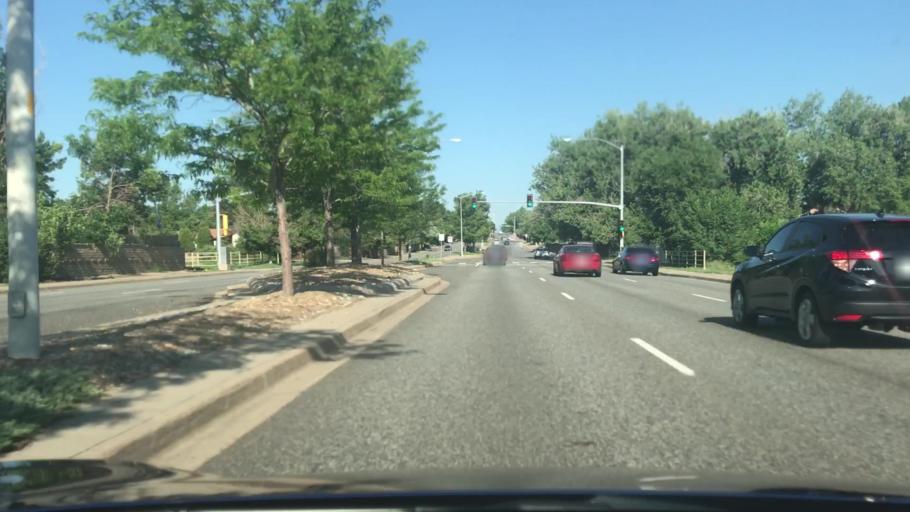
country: US
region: Colorado
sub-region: Arapahoe County
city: Dove Valley
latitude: 39.6531
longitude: -104.7969
